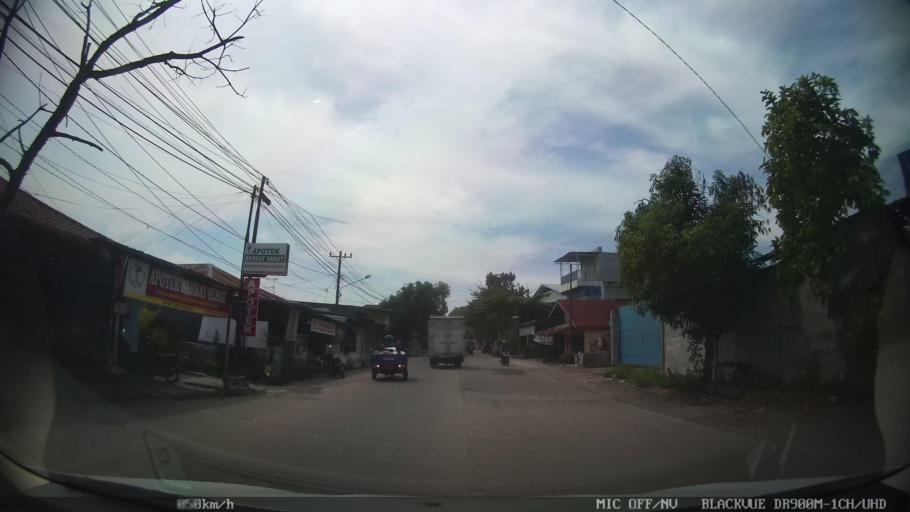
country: ID
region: North Sumatra
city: Labuhan Deli
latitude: 3.6691
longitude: 98.6792
